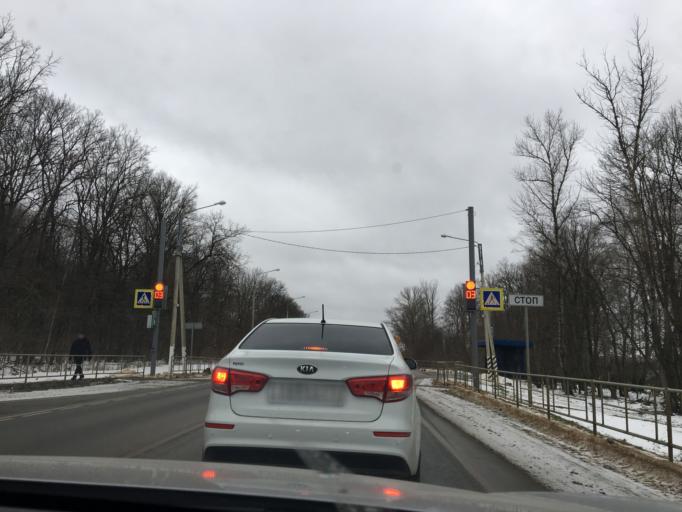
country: RU
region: Tula
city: Pervomayskiy
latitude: 54.0719
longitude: 37.5399
